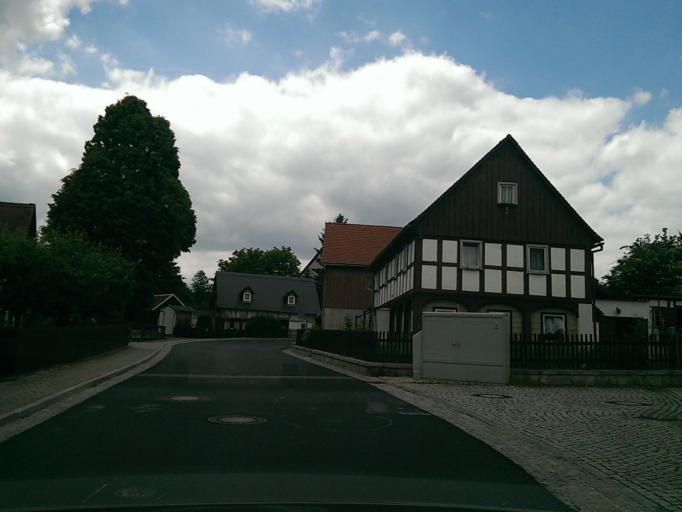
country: DE
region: Saxony
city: Bertsdorf-Hoernitz
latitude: 50.8781
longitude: 14.7171
